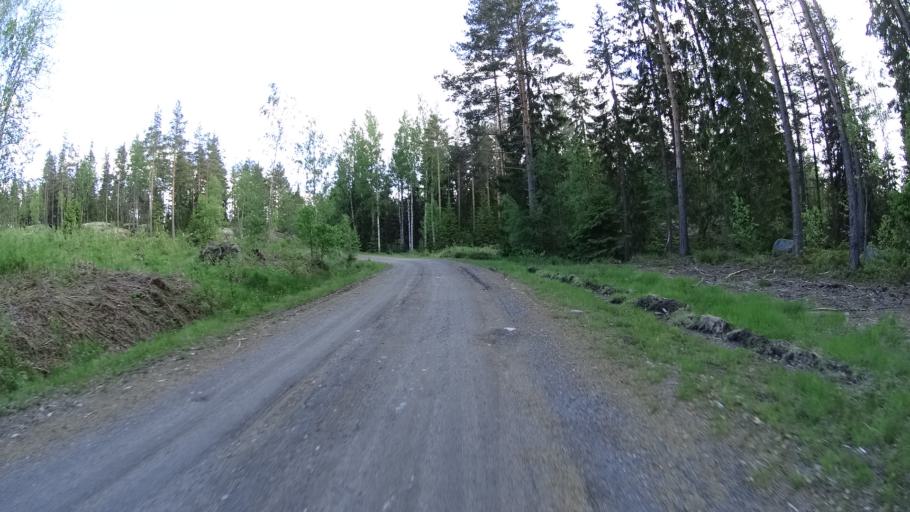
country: FI
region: Varsinais-Suomi
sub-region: Salo
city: Kisko
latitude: 60.1622
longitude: 23.4901
